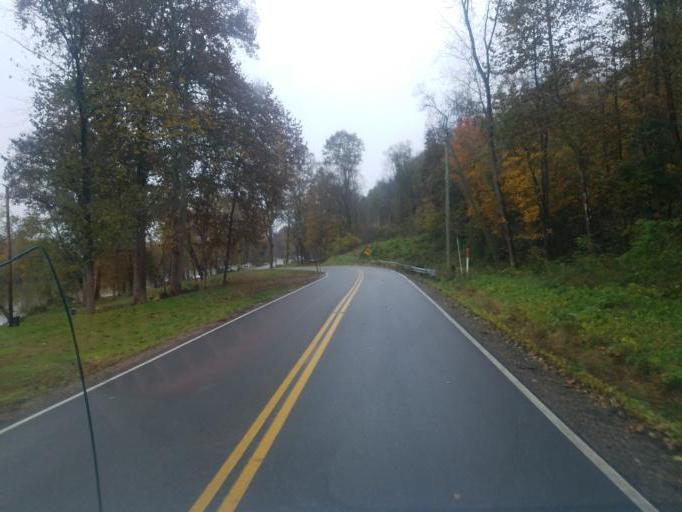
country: US
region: Ohio
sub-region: Morgan County
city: McConnelsville
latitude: 39.6129
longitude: -81.8335
